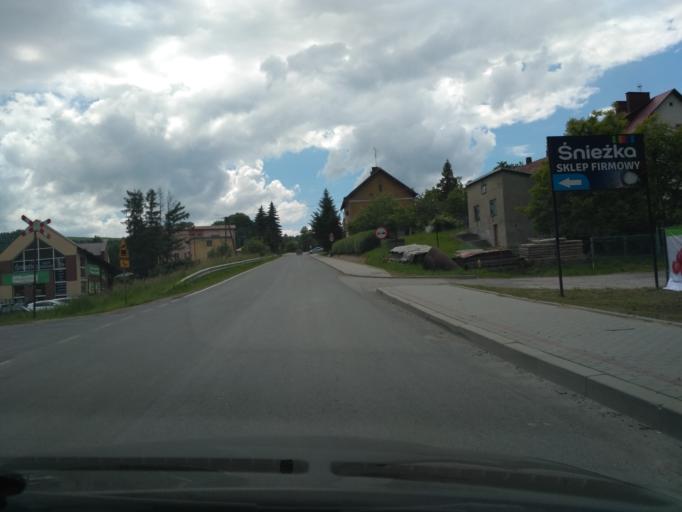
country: PL
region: Subcarpathian Voivodeship
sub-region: Powiat przeworski
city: Jawornik Polski
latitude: 49.8926
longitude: 22.2906
